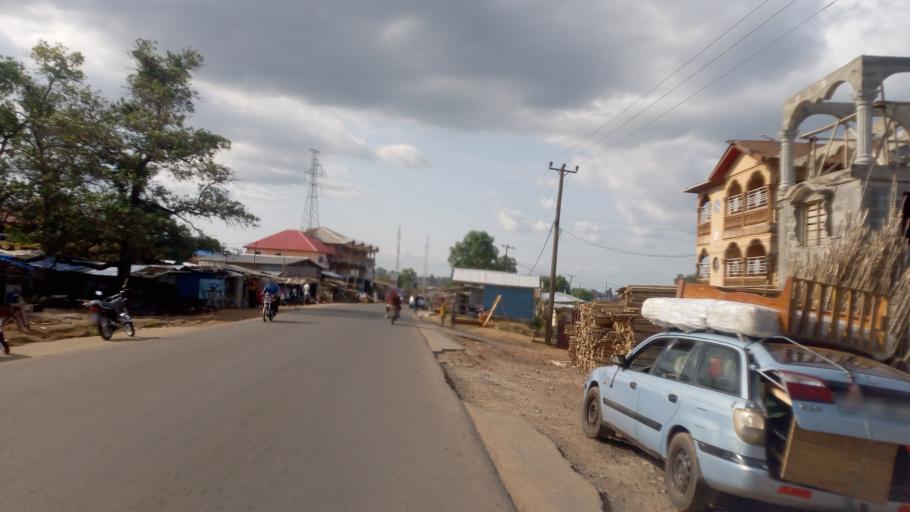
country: SL
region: Western Area
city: Waterloo
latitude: 8.3253
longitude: -13.0724
